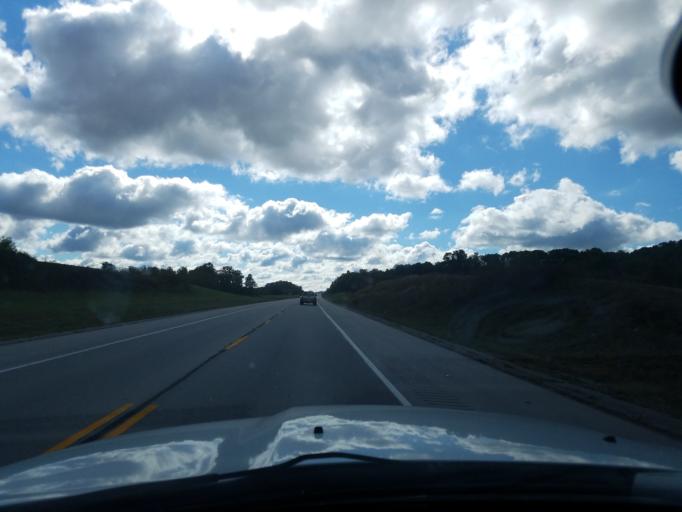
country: US
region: Kentucky
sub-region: Rockcastle County
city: Brodhead
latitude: 37.4075
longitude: -84.4362
